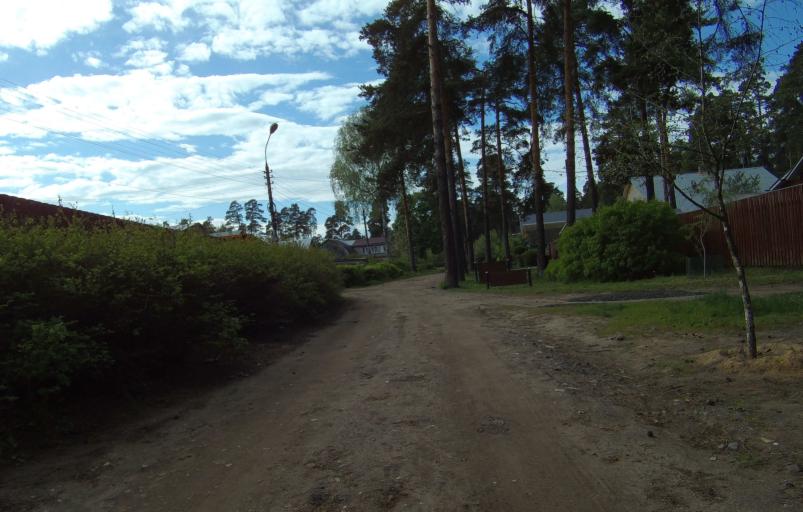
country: RU
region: Moskovskaya
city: Kratovo
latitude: 55.5733
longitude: 38.1922
